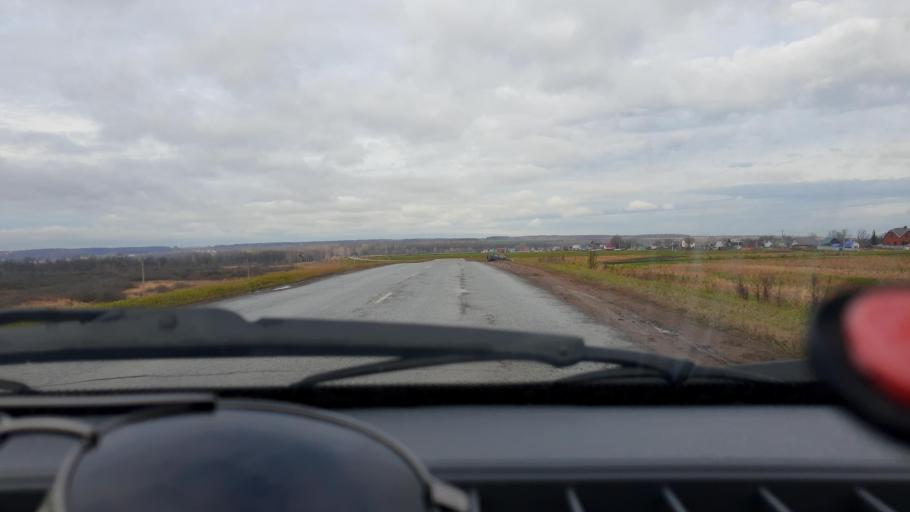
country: RU
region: Bashkortostan
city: Mikhaylovka
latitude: 54.8299
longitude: 55.9629
